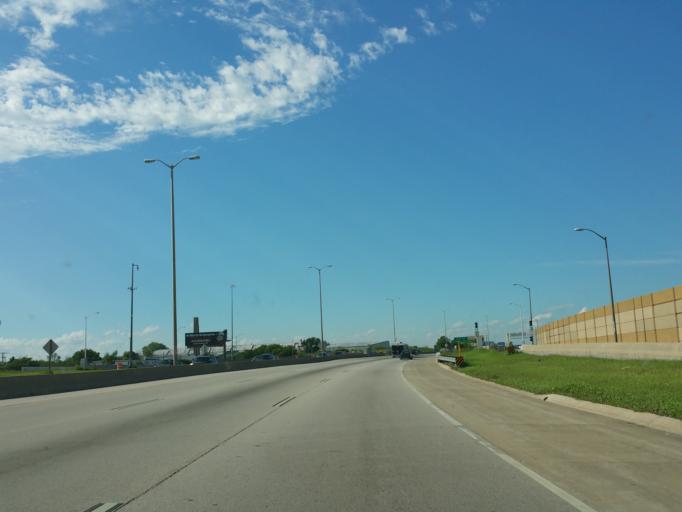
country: US
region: Wisconsin
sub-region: Milwaukee County
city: Saint Francis
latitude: 42.9807
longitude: -87.9163
